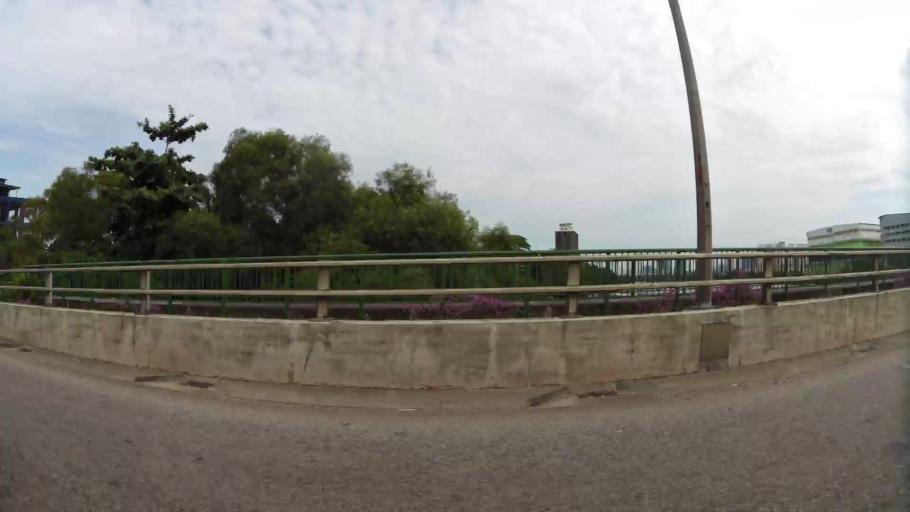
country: SG
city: Singapore
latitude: 1.3132
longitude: 103.7264
